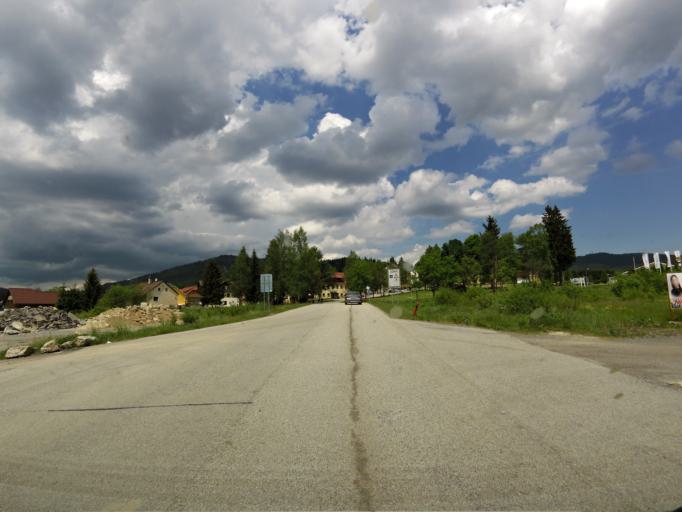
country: DE
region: Bavaria
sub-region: Lower Bavaria
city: Philippsreut
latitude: 48.9062
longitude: 13.7216
